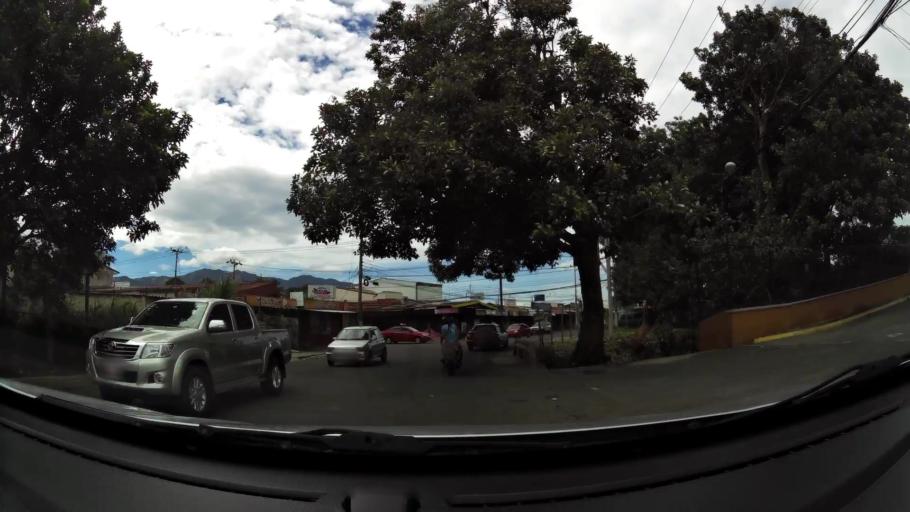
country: CR
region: San Jose
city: Patarra
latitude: 9.8926
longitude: -84.0530
